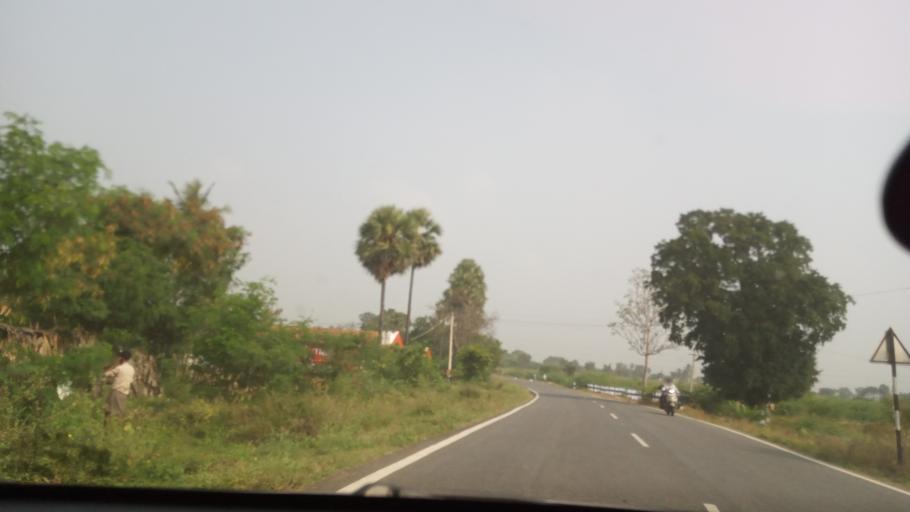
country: IN
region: Tamil Nadu
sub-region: Erode
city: Punjai Puliyampatti
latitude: 11.3883
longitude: 77.1782
